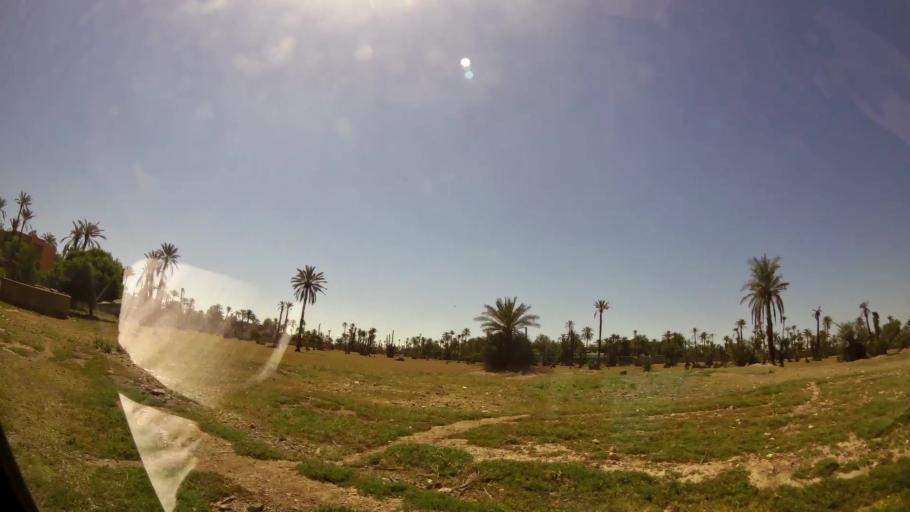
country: MA
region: Marrakech-Tensift-Al Haouz
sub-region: Marrakech
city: Marrakesh
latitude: 31.6786
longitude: -7.9788
